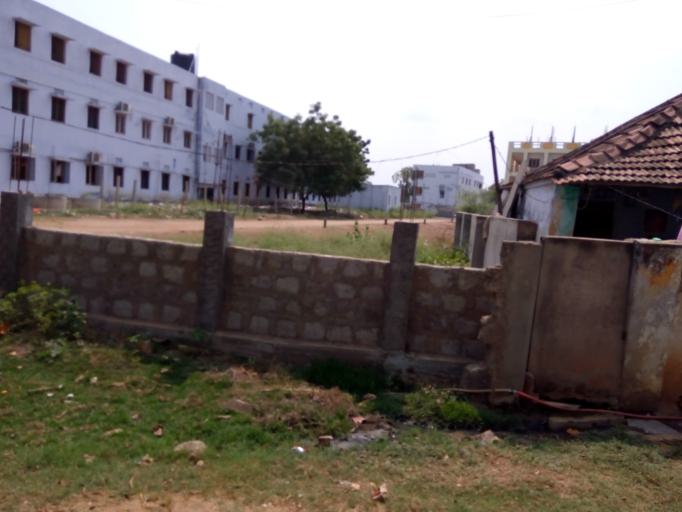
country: IN
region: Andhra Pradesh
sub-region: Prakasam
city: pedda nakkalapalem
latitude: 15.9672
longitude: 80.2734
